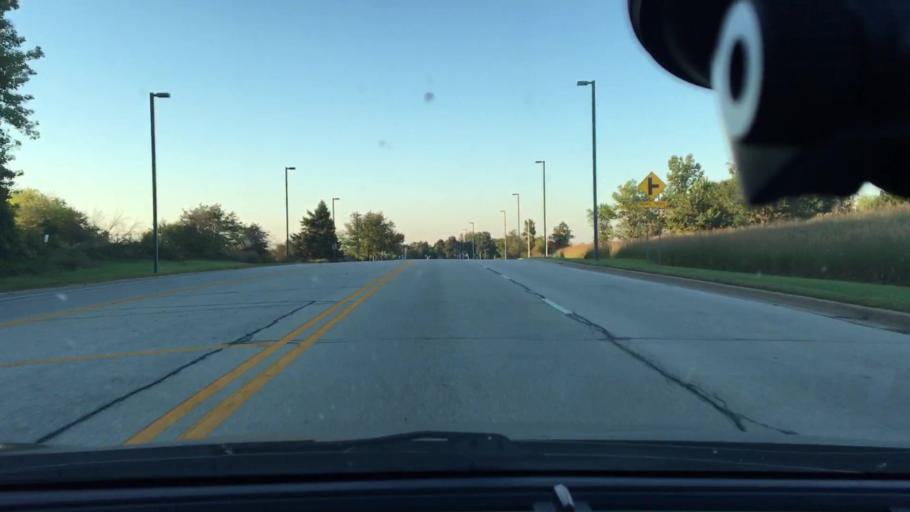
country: US
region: Illinois
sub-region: Kane County
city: East Dundee
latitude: 42.0762
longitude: -88.2236
